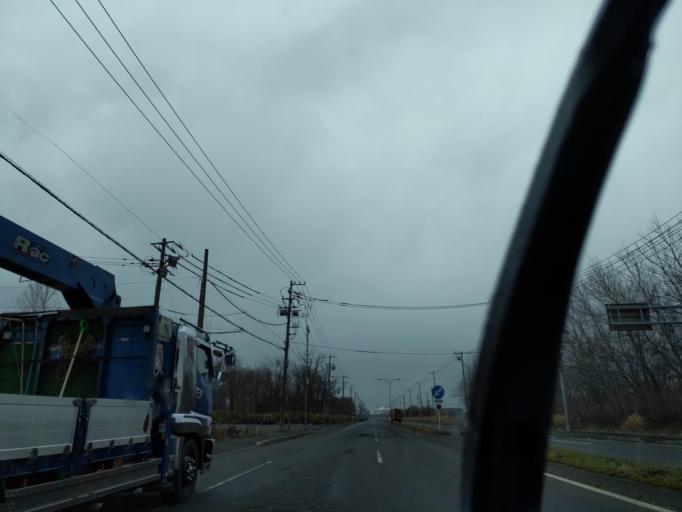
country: JP
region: Hokkaido
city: Ishikari
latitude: 43.1804
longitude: 141.2981
